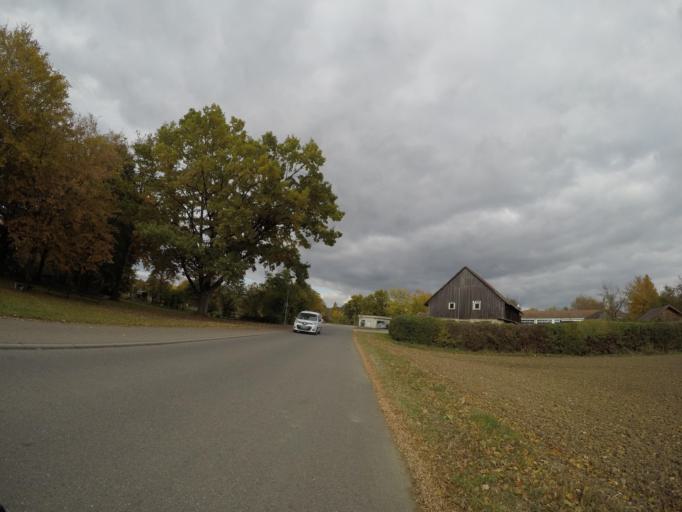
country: DE
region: Baden-Wuerttemberg
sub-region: Tuebingen Region
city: Munderkingen
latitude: 48.2330
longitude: 9.6492
